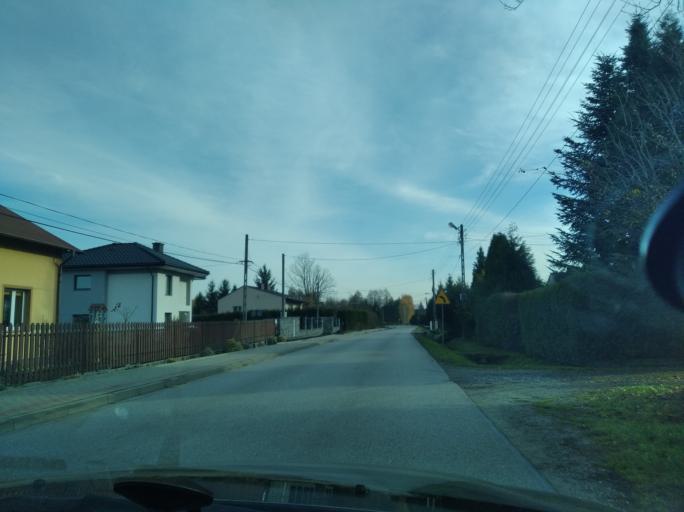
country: PL
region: Subcarpathian Voivodeship
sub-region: Powiat lancucki
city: Kraczkowa
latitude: 50.0367
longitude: 22.1417
